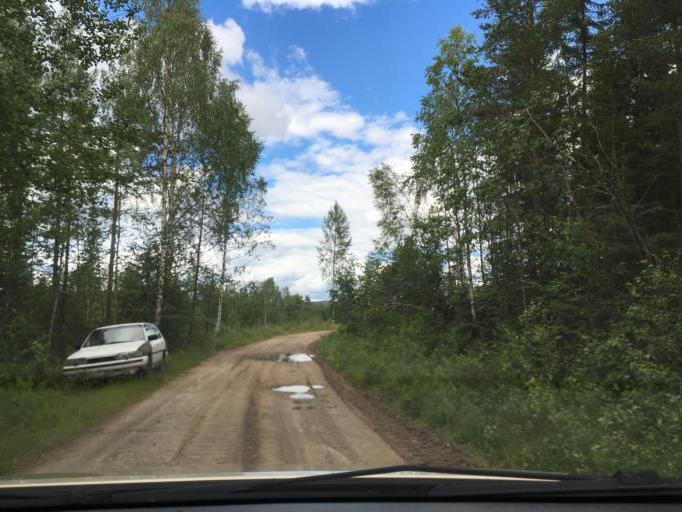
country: SE
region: Norrbotten
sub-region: Overkalix Kommun
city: OEverkalix
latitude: 66.1384
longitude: 22.7837
